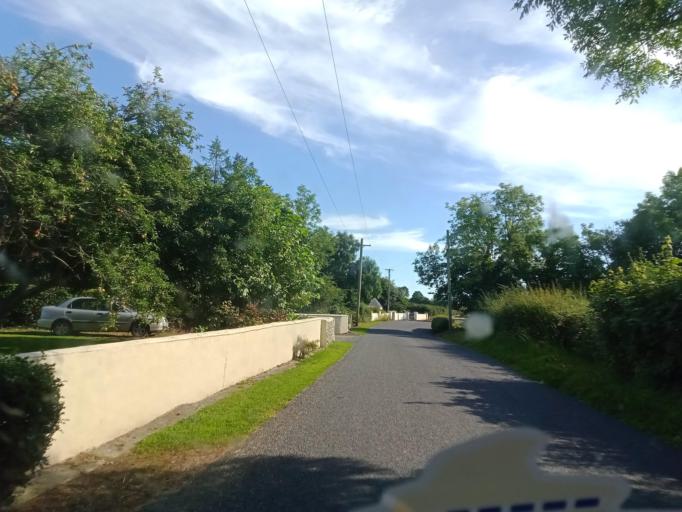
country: IE
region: Leinster
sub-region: Kilkenny
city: Ballyragget
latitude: 52.7736
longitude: -7.3882
